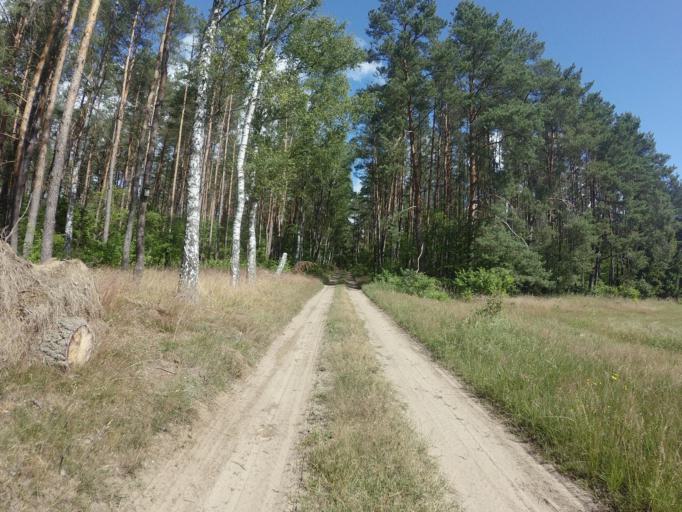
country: PL
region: West Pomeranian Voivodeship
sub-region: Powiat choszczenski
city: Recz
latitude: 53.2734
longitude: 15.6582
